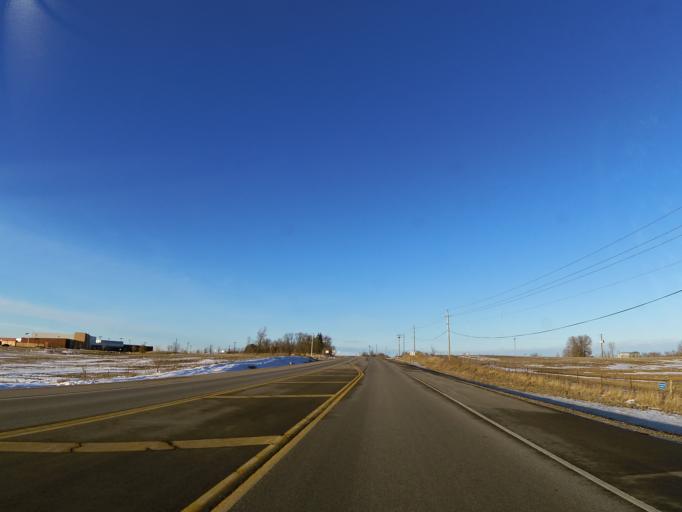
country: US
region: Minnesota
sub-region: Washington County
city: Cottage Grove
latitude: 44.8602
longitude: -92.9028
